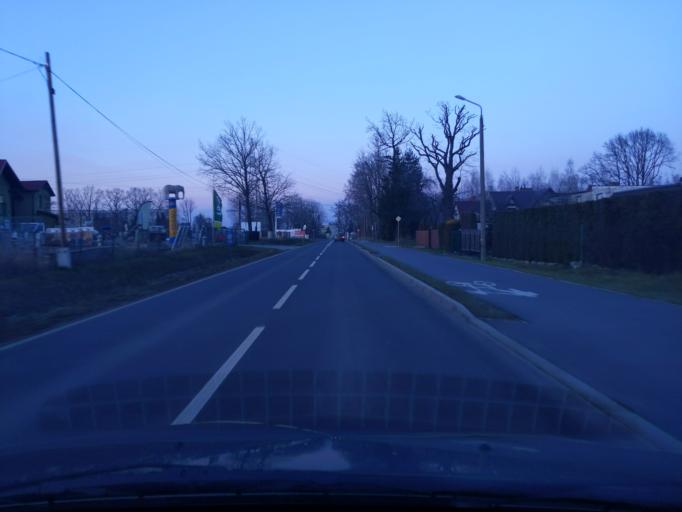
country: PL
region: Silesian Voivodeship
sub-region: Powiat pszczynski
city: Pszczyna
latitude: 49.9584
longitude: 18.9330
